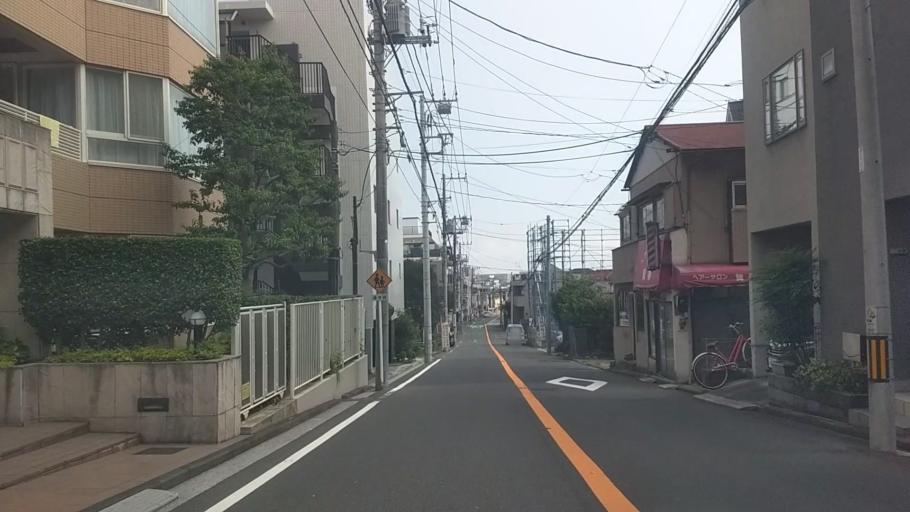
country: JP
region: Kanagawa
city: Yokohama
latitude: 35.4942
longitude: 139.6385
